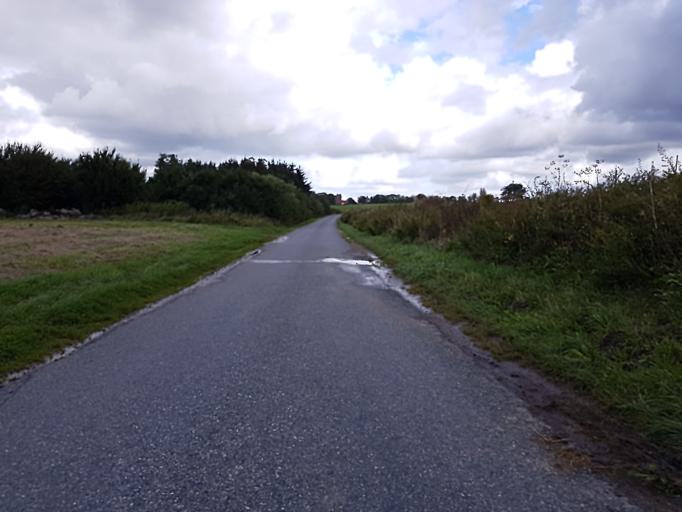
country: DK
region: Zealand
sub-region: Roskilde Kommune
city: Gundsomagle
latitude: 55.7171
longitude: 12.1487
